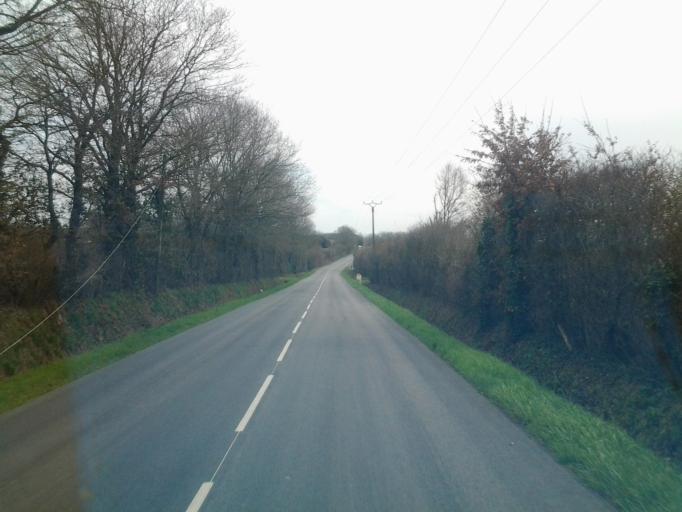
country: FR
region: Pays de la Loire
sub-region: Departement de la Vendee
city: La Roche-sur-Yon
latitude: 46.6704
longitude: -1.4736
